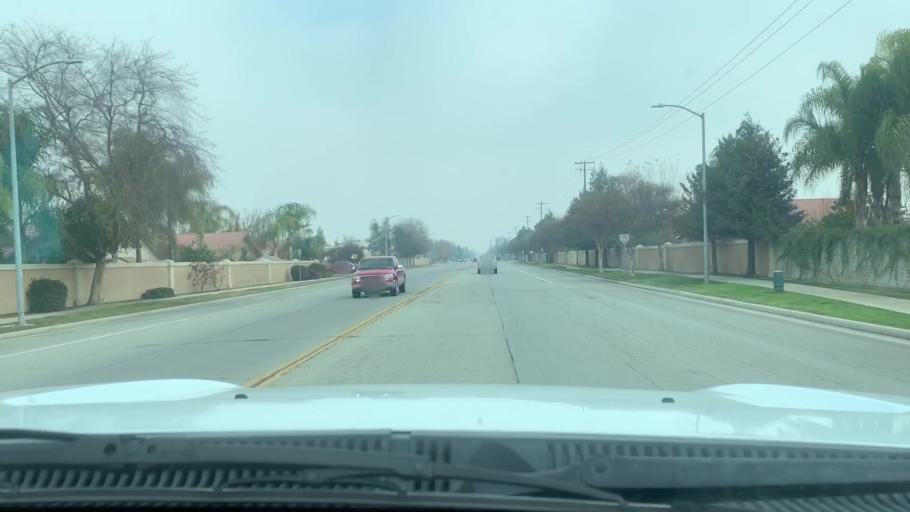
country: US
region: California
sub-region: Kern County
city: Shafter
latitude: 35.4999
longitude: -119.2919
